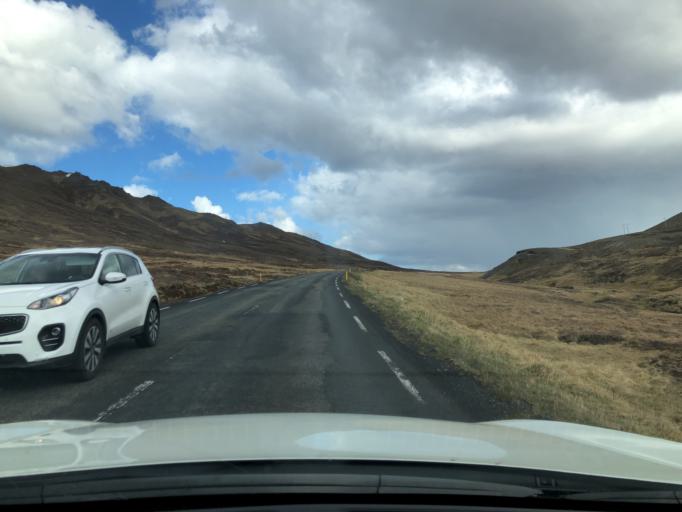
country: IS
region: West
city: Stykkisholmur
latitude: 64.9669
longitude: -23.0145
